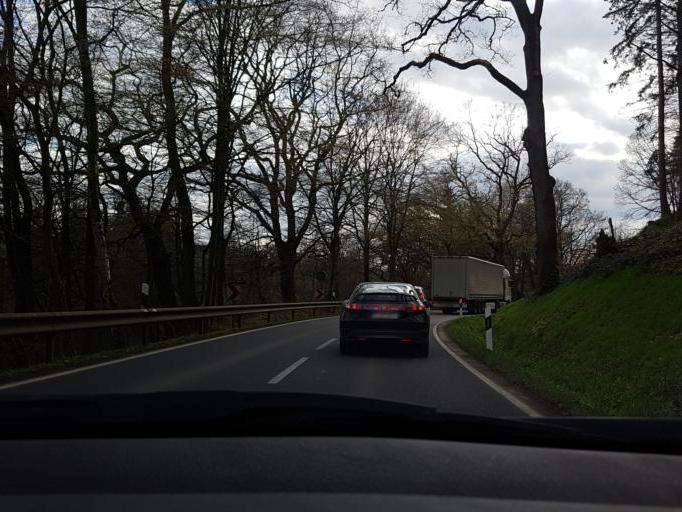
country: DE
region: Lower Saxony
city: Bodenfelde
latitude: 51.6275
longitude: 9.5789
